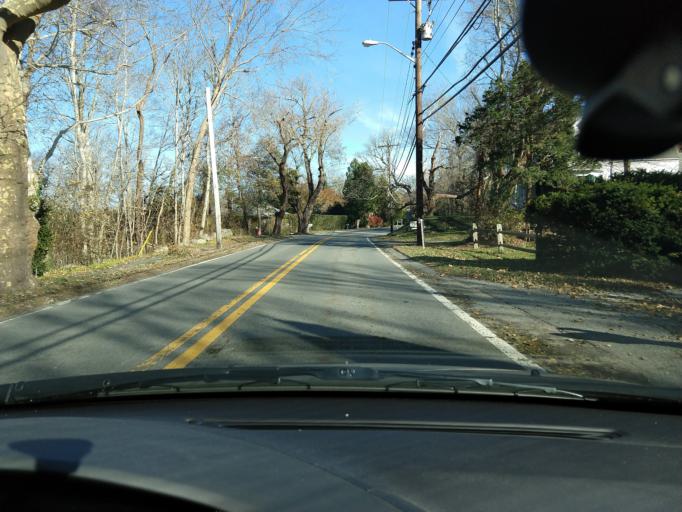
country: US
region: Massachusetts
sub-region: Barnstable County
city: Barnstable
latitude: 41.6985
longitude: -70.3340
